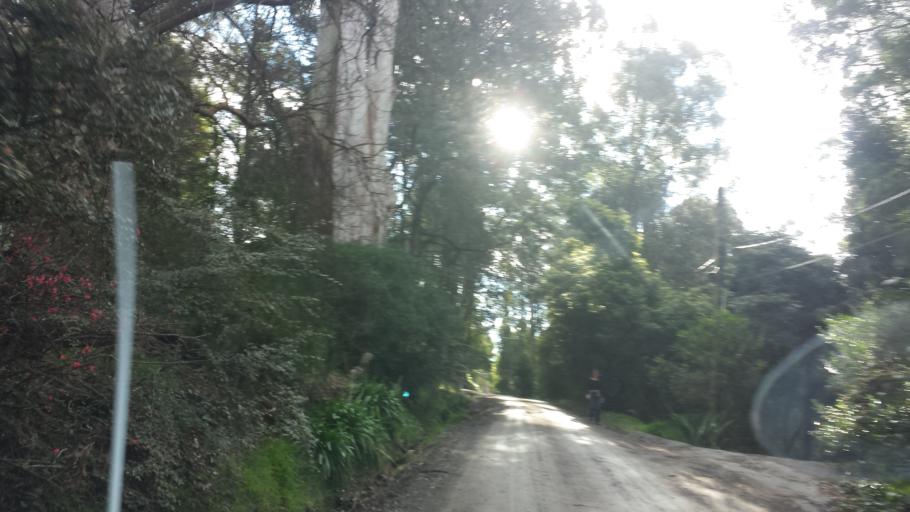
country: AU
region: Victoria
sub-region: Yarra Ranges
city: Kallista
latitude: -37.8836
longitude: 145.3791
